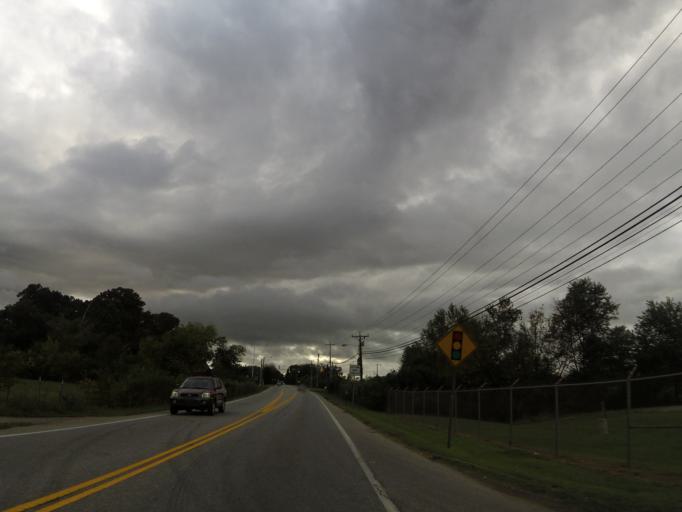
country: US
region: Tennessee
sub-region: Blount County
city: Alcoa
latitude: 35.8059
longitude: -83.9747
